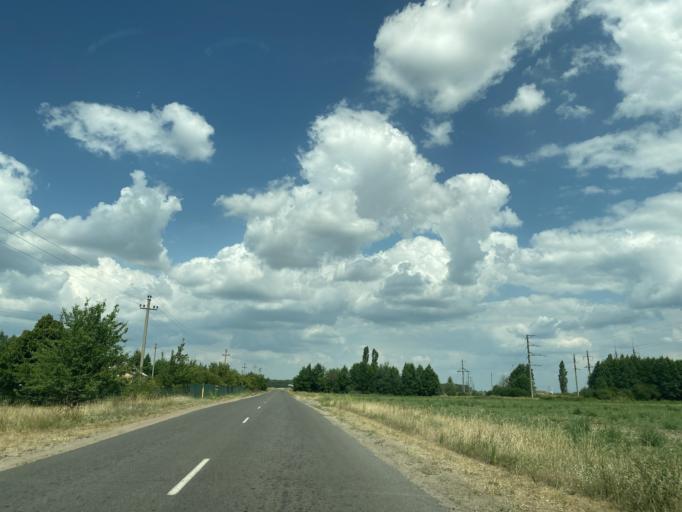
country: BY
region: Brest
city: Ivanava
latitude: 52.3501
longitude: 25.6292
